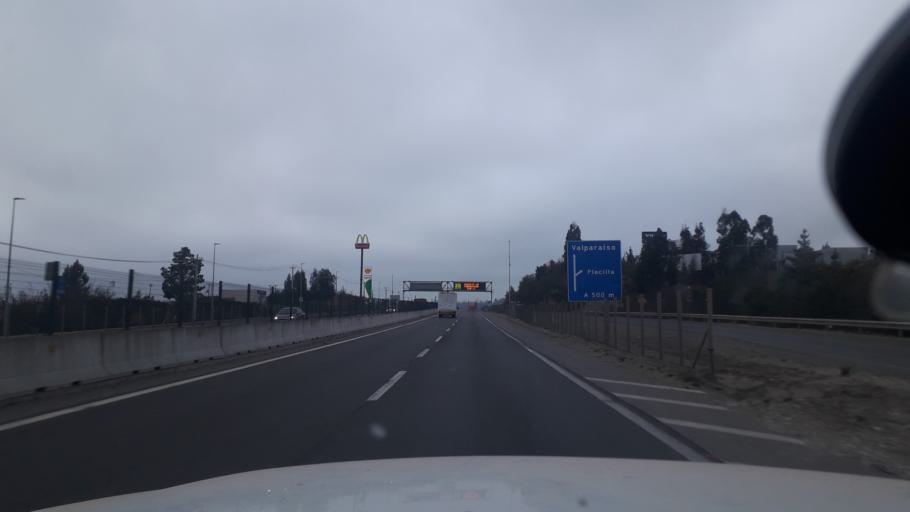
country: CL
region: Valparaiso
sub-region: Provincia de Valparaiso
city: Vina del Mar
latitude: -33.1247
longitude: -71.5613
